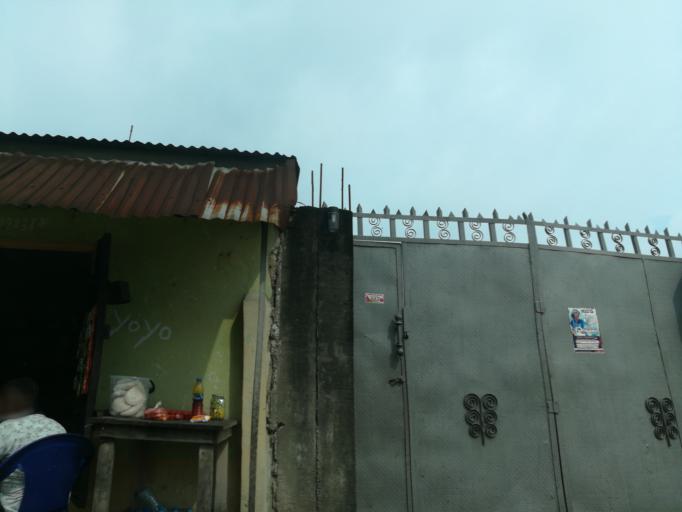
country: NG
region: Rivers
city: Port Harcourt
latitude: 4.8712
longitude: 6.9859
